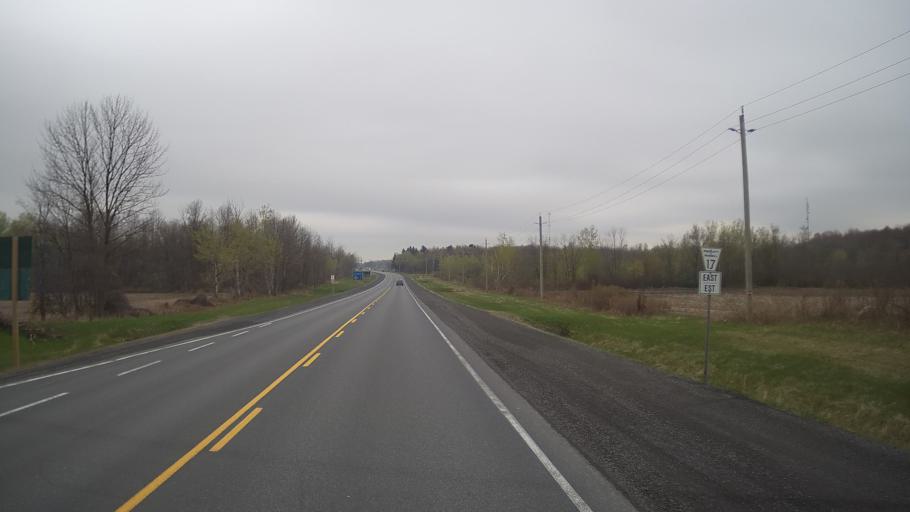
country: CA
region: Ontario
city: Hawkesbury
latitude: 45.5713
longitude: -74.5234
